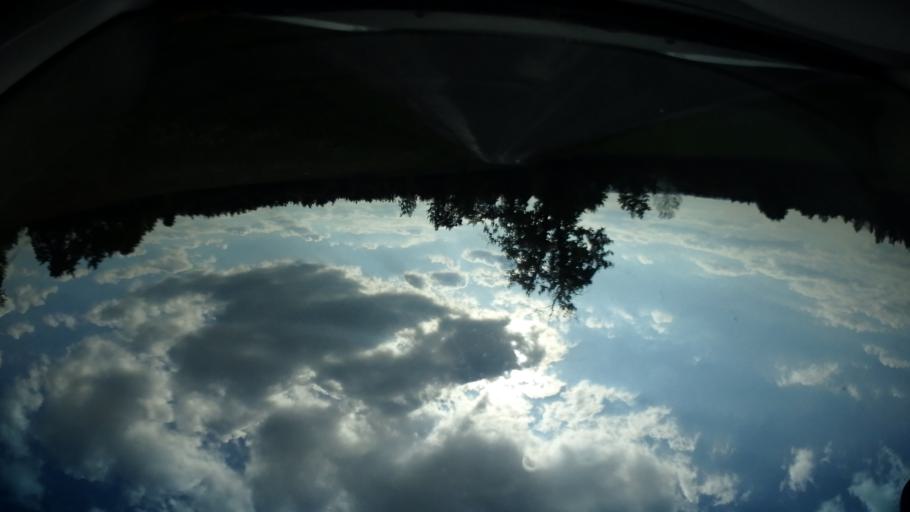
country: CZ
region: Vysocina
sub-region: Okres Zd'ar nad Sazavou
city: Velke Mezirici
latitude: 49.3488
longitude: 15.9594
